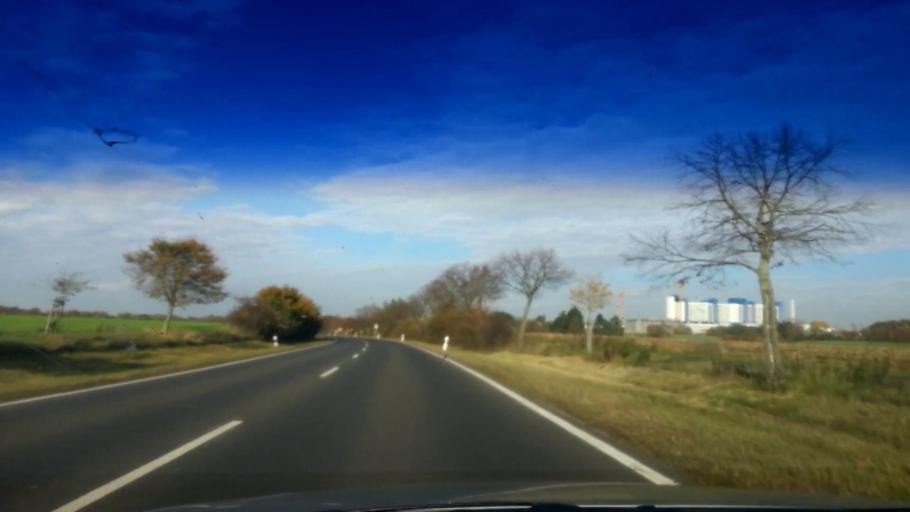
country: DE
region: Bavaria
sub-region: Upper Franconia
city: Stegaurach
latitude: 49.8619
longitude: 10.8814
